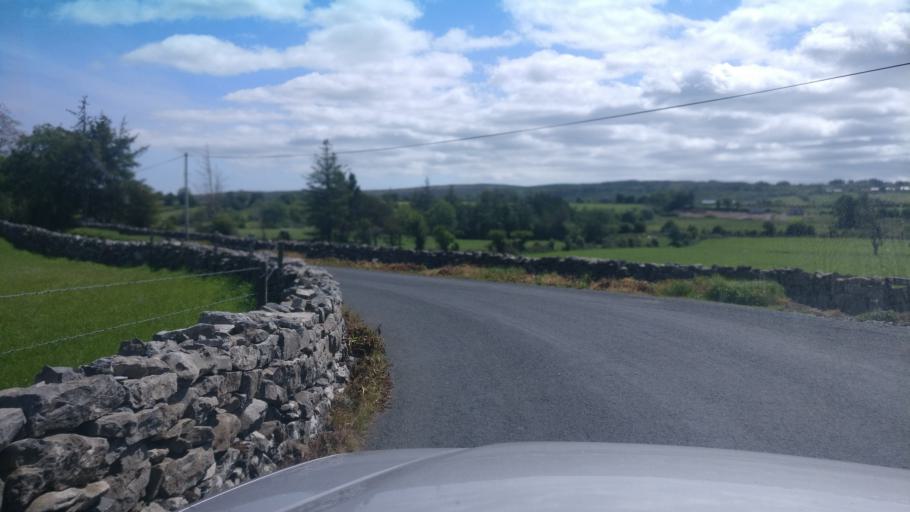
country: IE
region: Connaught
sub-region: County Galway
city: Gort
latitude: 53.1403
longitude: -8.7276
